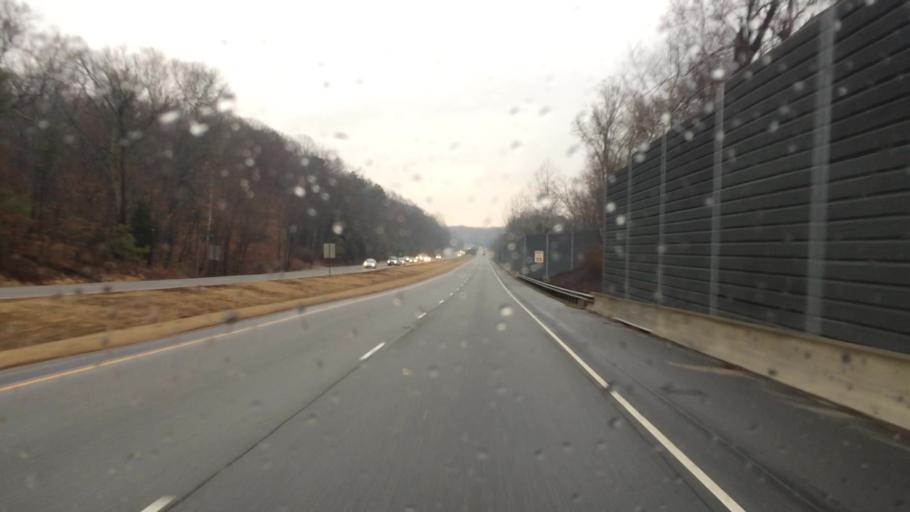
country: US
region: Virginia
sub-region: City of Williamsburg
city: Williamsburg
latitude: 37.2492
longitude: -76.7214
